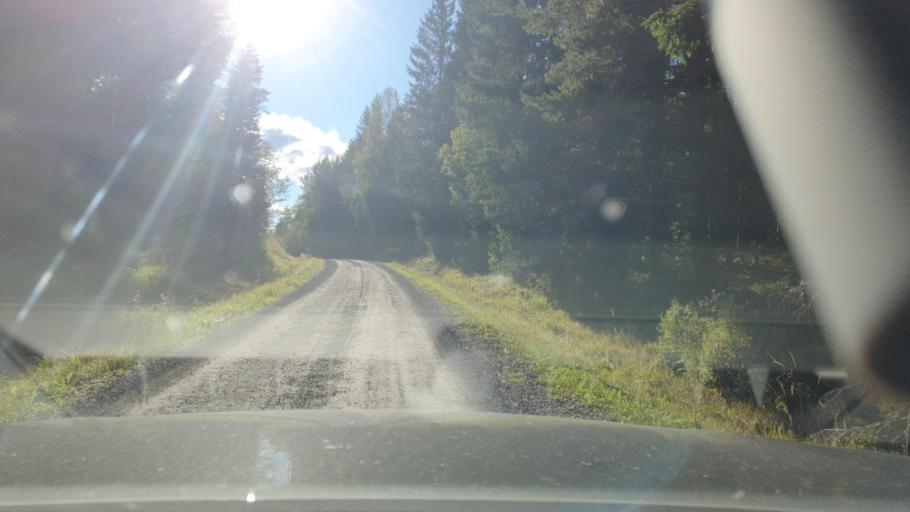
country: SE
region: Vaermland
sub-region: Filipstads Kommun
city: Filipstad
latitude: 59.8163
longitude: 13.9640
